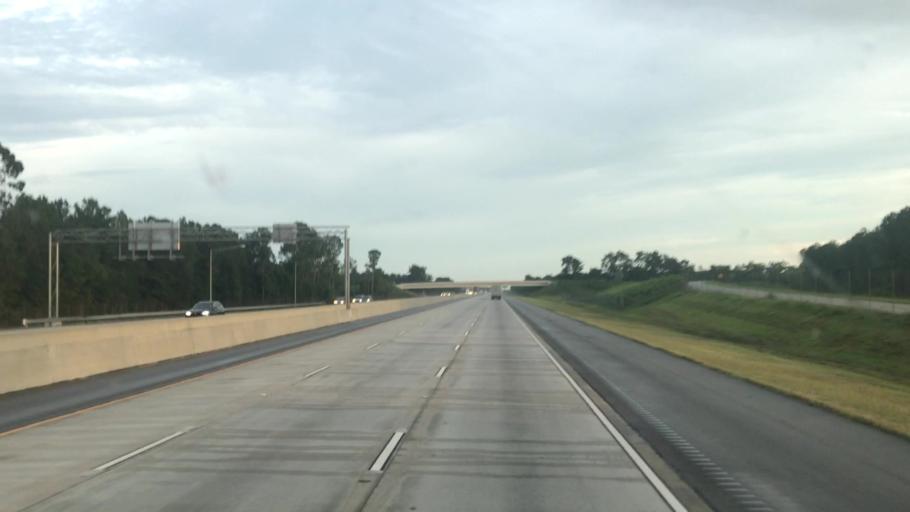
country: US
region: Georgia
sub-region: Cook County
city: Sparks
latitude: 31.2407
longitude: -83.4658
